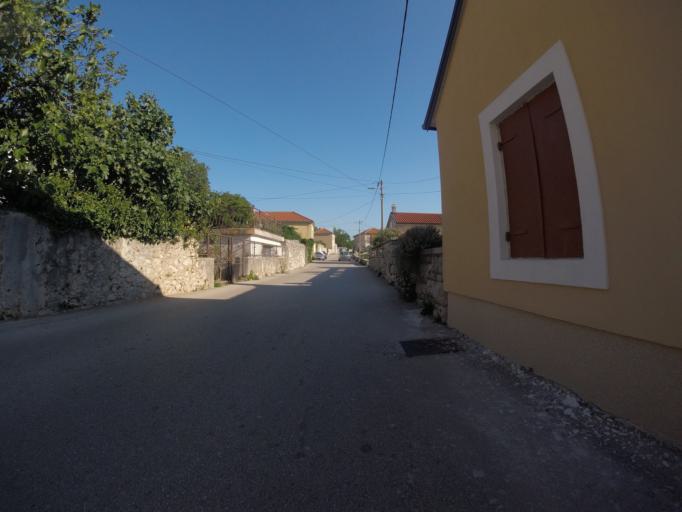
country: HR
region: Primorsko-Goranska
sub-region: Grad Crikvenica
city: Jadranovo
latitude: 45.2498
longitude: 14.6274
